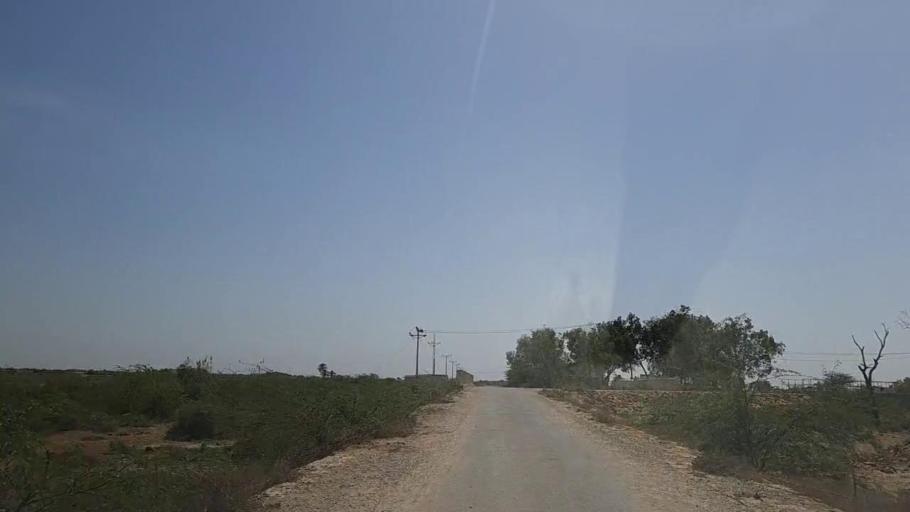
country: PK
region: Sindh
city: Gharo
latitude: 24.7717
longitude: 67.7529
